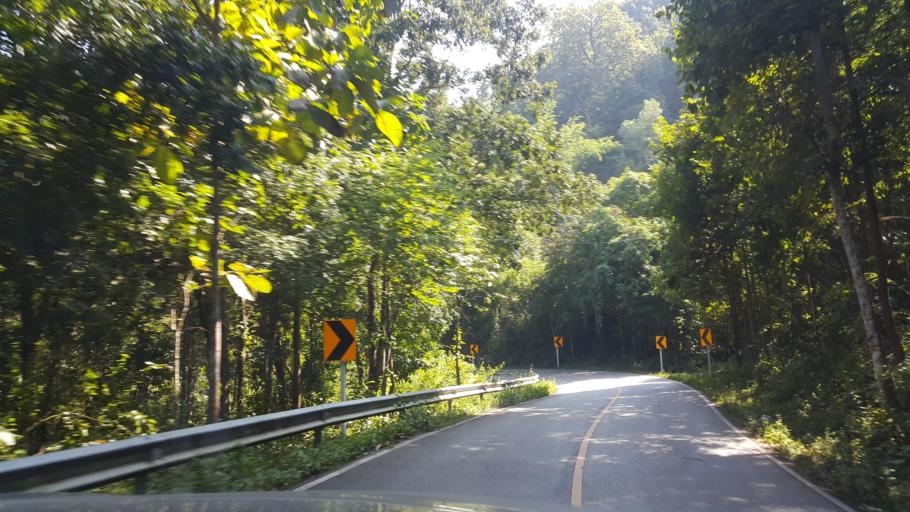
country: TH
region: Chiang Mai
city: Samoeng
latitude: 18.8556
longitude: 98.6750
